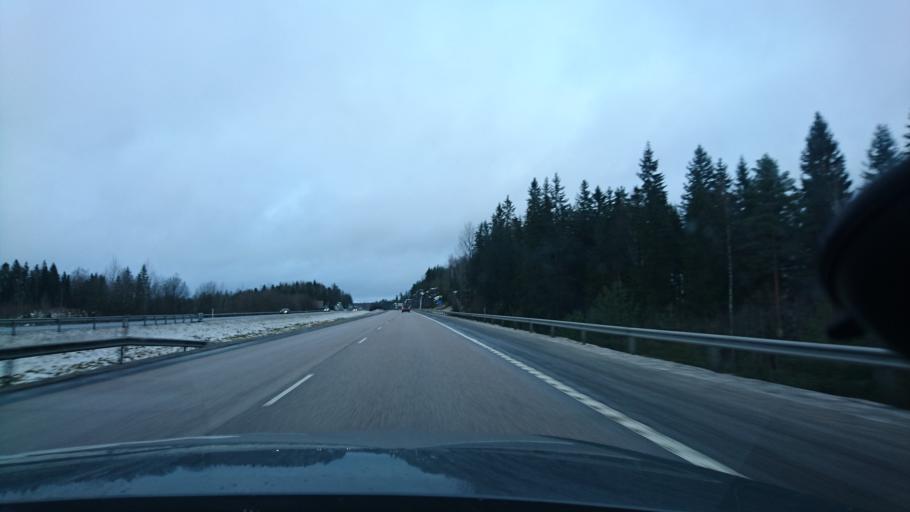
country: FI
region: Uusimaa
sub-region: Helsinki
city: Maentsaelae
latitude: 60.6824
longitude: 25.3797
